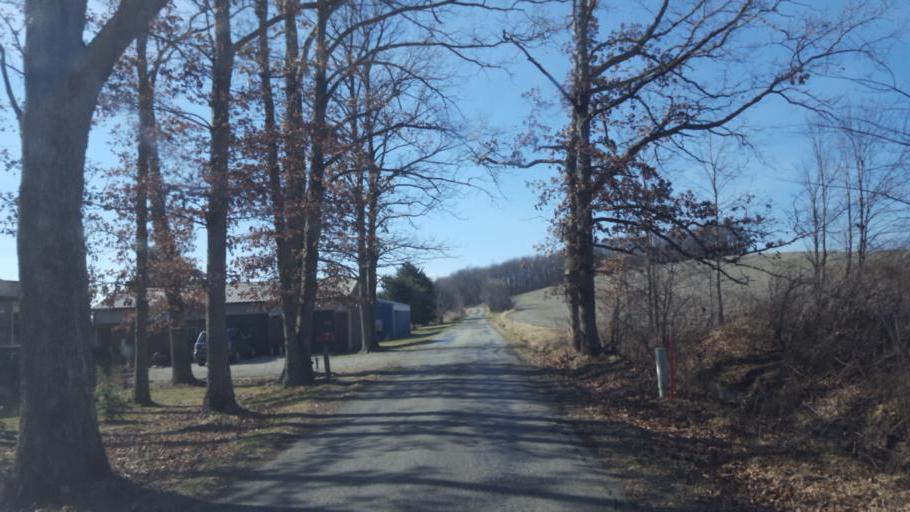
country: US
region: Ohio
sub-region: Knox County
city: Fredericktown
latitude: 40.5183
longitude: -82.4499
